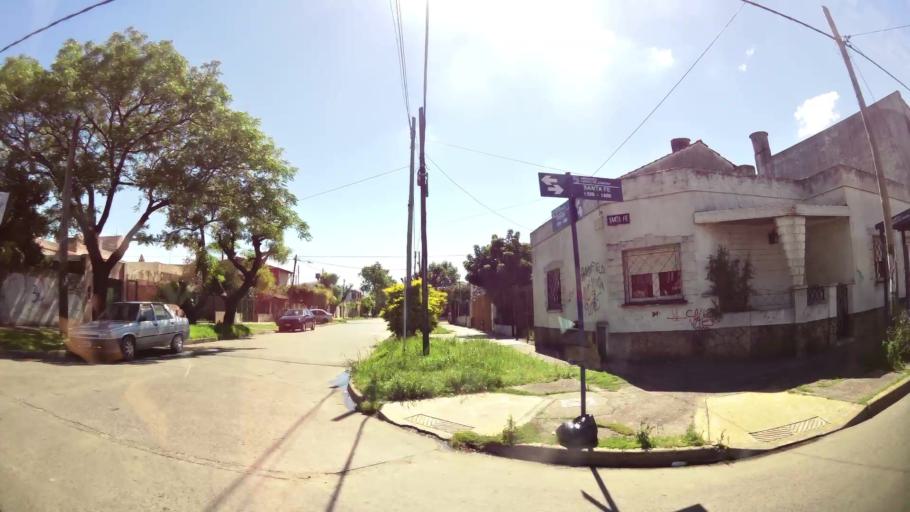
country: AR
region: Buenos Aires
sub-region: Partido de Lomas de Zamora
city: Lomas de Zamora
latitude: -34.7395
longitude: -58.4182
